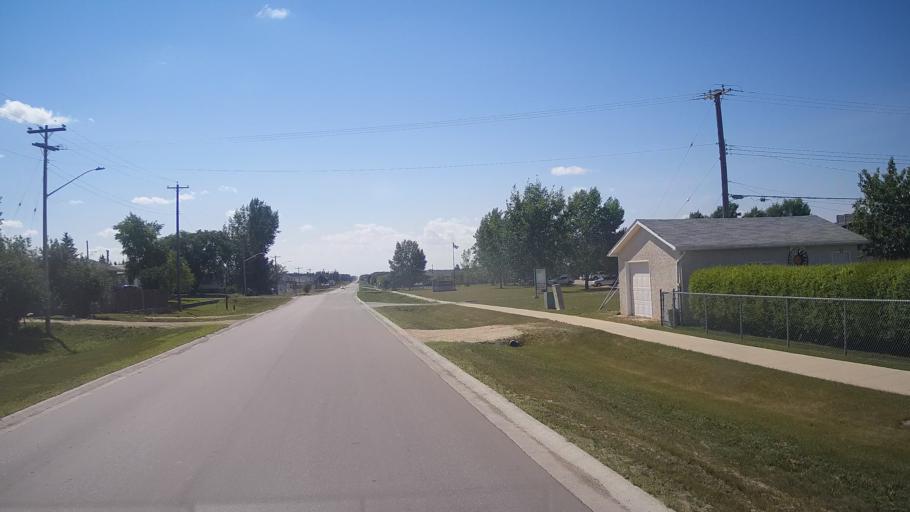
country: CA
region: Manitoba
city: Stonewall
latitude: 50.1302
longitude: -97.3341
